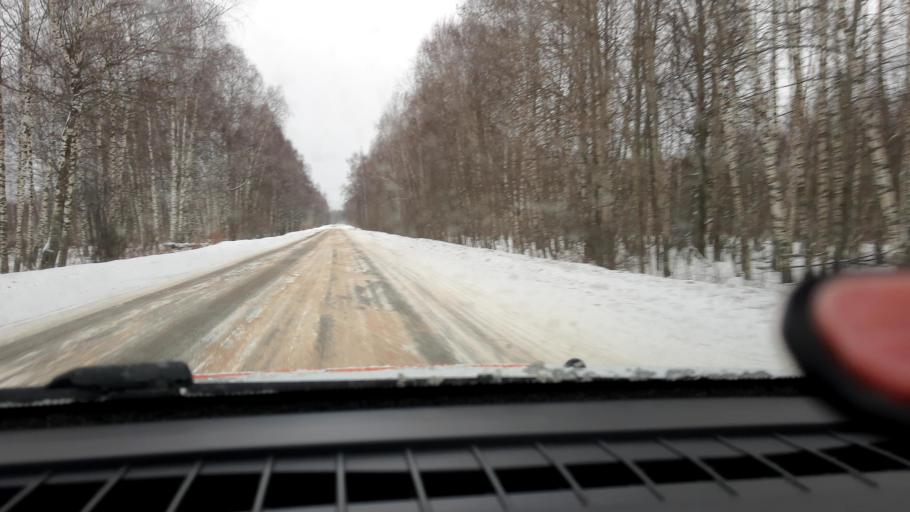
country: RU
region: Nizjnij Novgorod
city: Pamyat' Parizhskoy Kommuny
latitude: 56.2408
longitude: 44.5120
